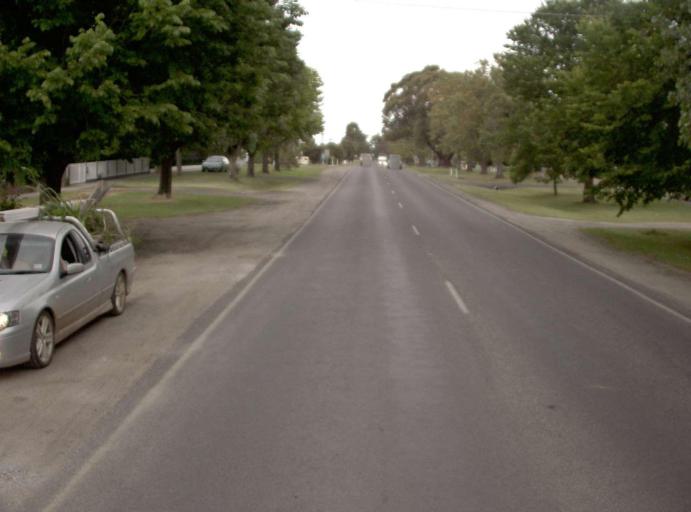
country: AU
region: Victoria
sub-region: Latrobe
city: Traralgon
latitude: -38.5678
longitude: 146.6750
